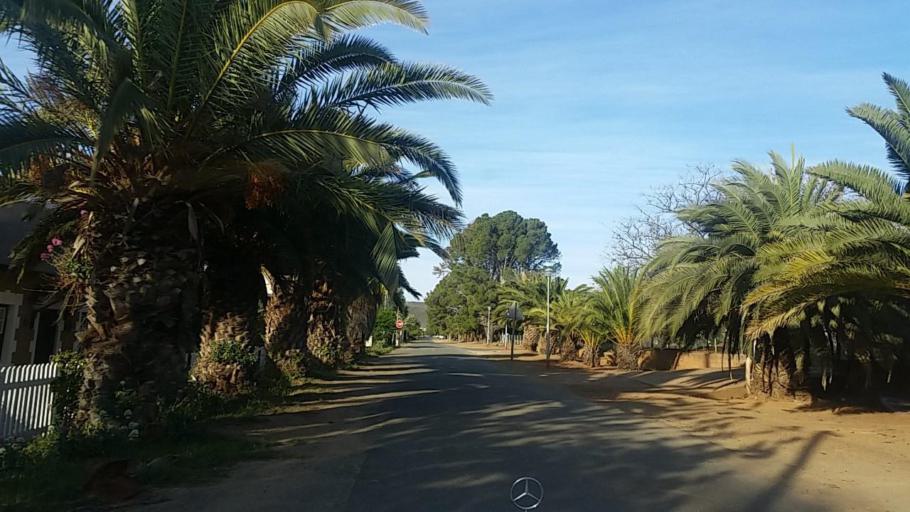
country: ZA
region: Western Cape
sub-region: Eden District Municipality
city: Knysna
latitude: -33.6555
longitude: 23.1255
